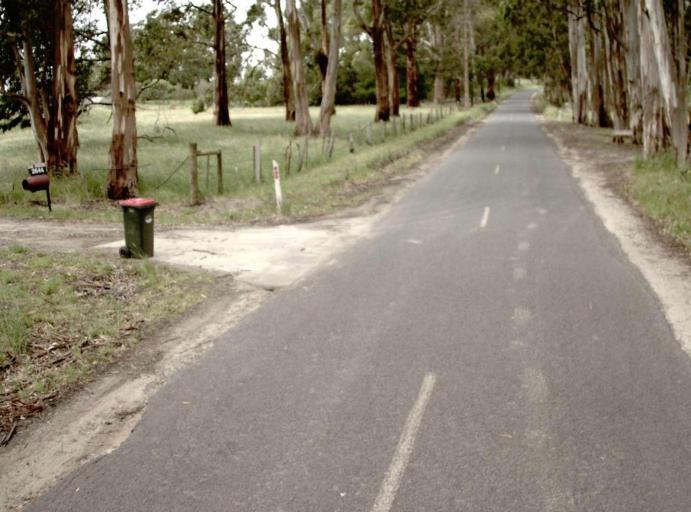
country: AU
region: Victoria
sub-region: Latrobe
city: Moe
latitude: -37.9908
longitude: 146.1455
